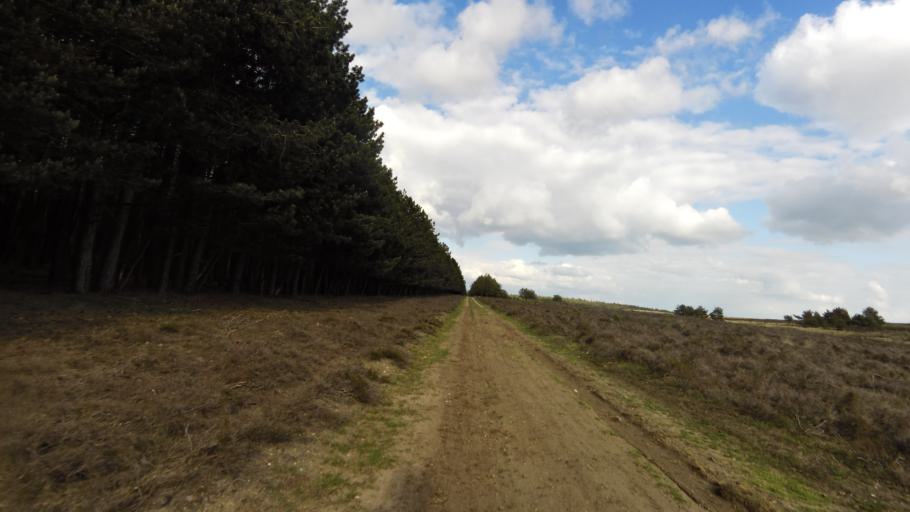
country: NL
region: Gelderland
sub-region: Gemeente Rozendaal
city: Rozendaal
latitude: 52.0617
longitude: 5.9564
